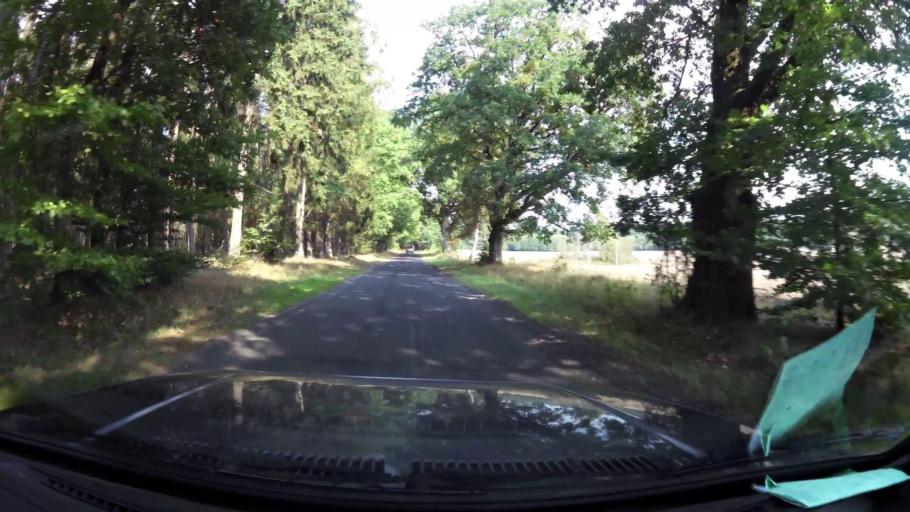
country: PL
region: West Pomeranian Voivodeship
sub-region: Powiat koszalinski
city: Bobolice
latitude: 54.0939
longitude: 16.4872
